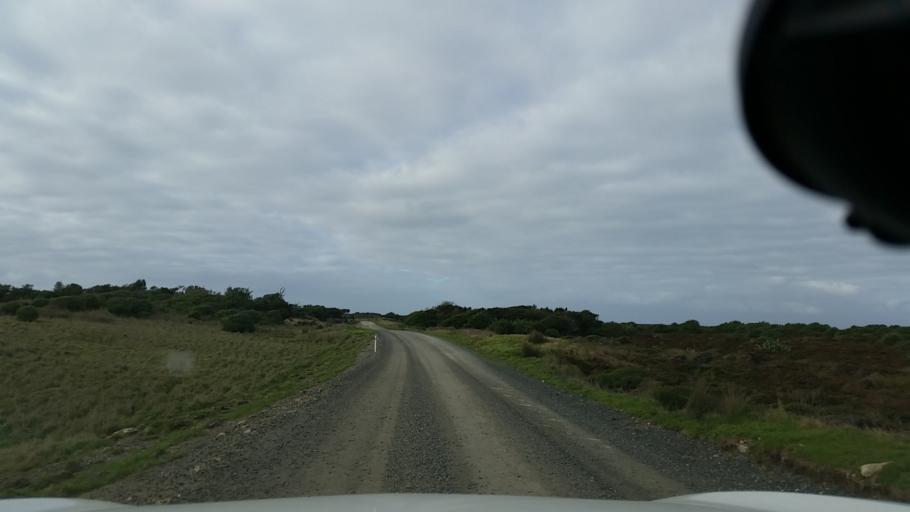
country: NZ
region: Chatham Islands
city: Waitangi
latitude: -43.7473
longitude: -176.3743
